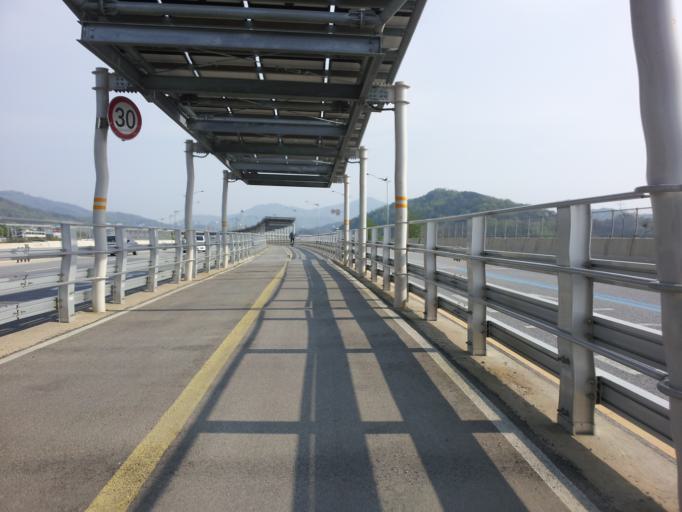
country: KR
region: Daejeon
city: Songgang-dong
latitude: 36.4659
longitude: 127.2751
